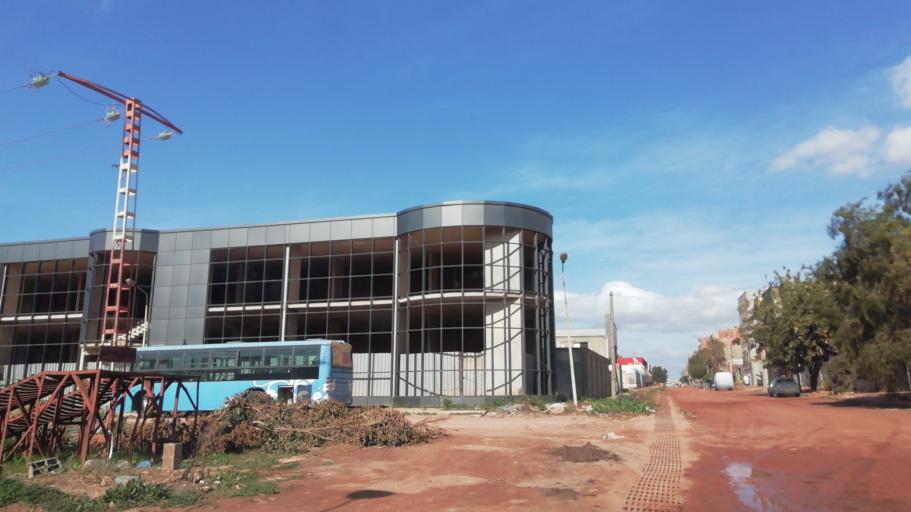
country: DZ
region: Oran
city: Es Senia
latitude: 35.6185
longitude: -0.5834
